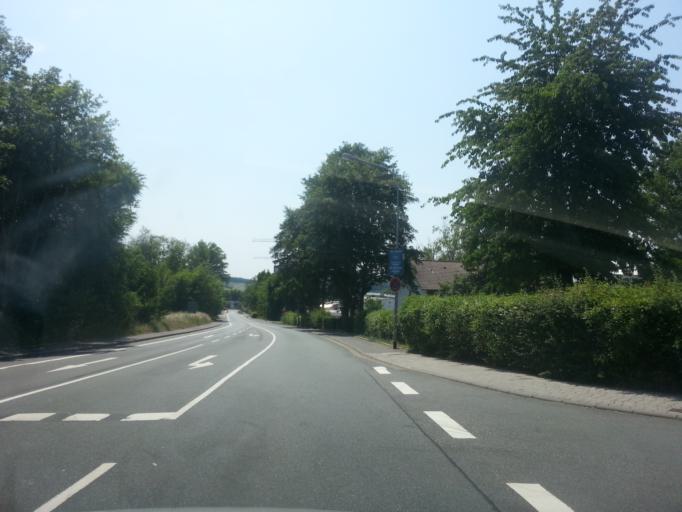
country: DE
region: Hesse
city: Ober-Ramstadt
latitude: 49.8377
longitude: 8.7430
